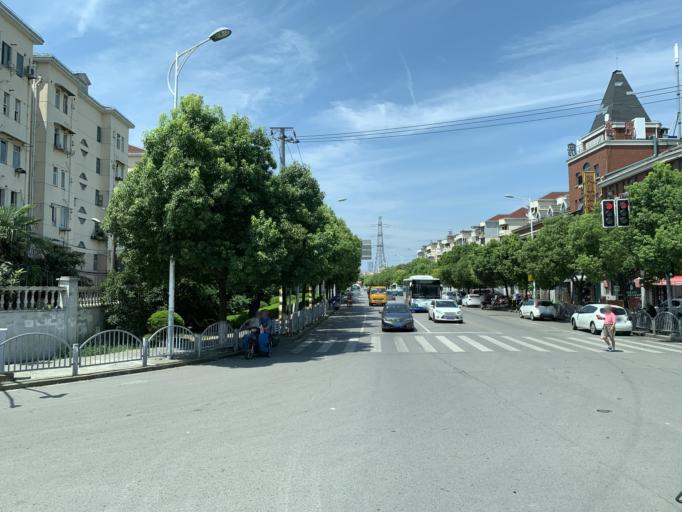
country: CN
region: Shanghai Shi
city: Huamu
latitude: 31.1725
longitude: 121.5368
